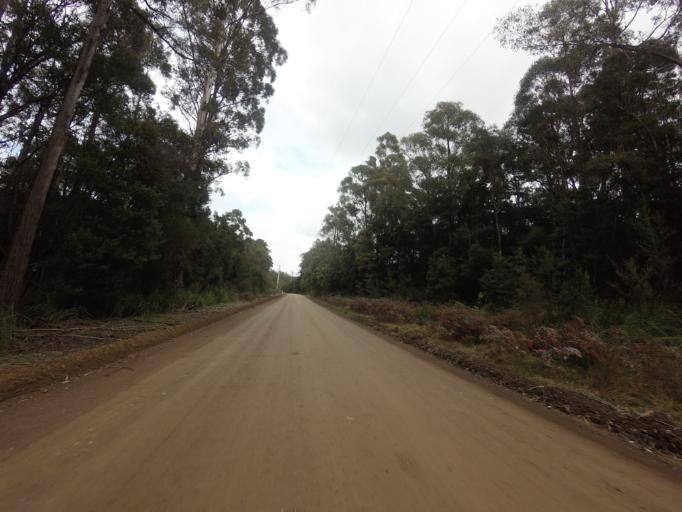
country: AU
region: Tasmania
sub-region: Huon Valley
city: Geeveston
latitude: -43.4131
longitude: 146.8984
